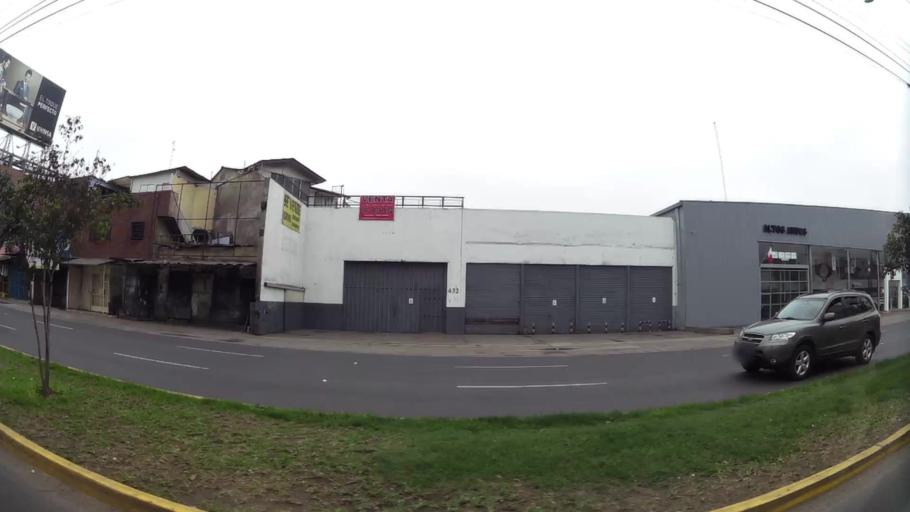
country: PE
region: Lima
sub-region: Lima
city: Surco
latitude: -12.1079
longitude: -77.0156
